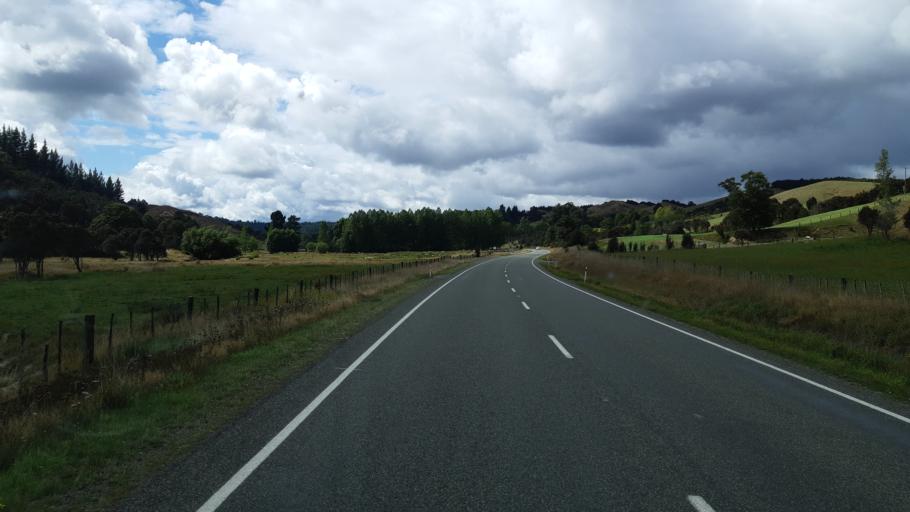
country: NZ
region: Tasman
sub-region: Tasman District
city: Wakefield
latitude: -41.6411
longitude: 172.6688
